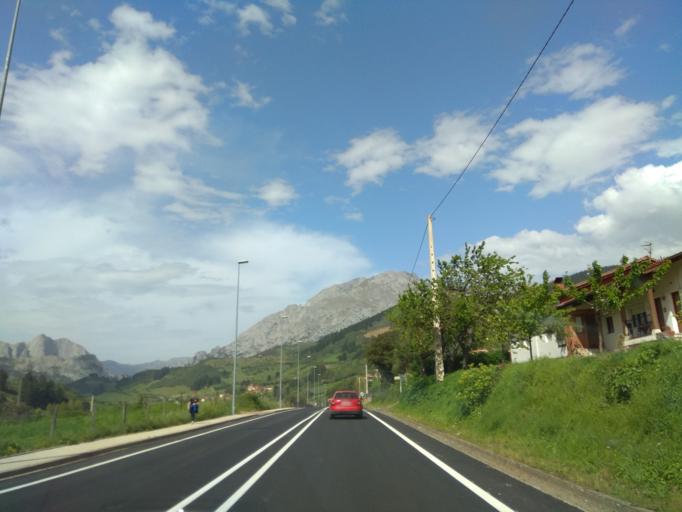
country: ES
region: Cantabria
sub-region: Provincia de Cantabria
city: Potes
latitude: 43.1676
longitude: -4.6055
